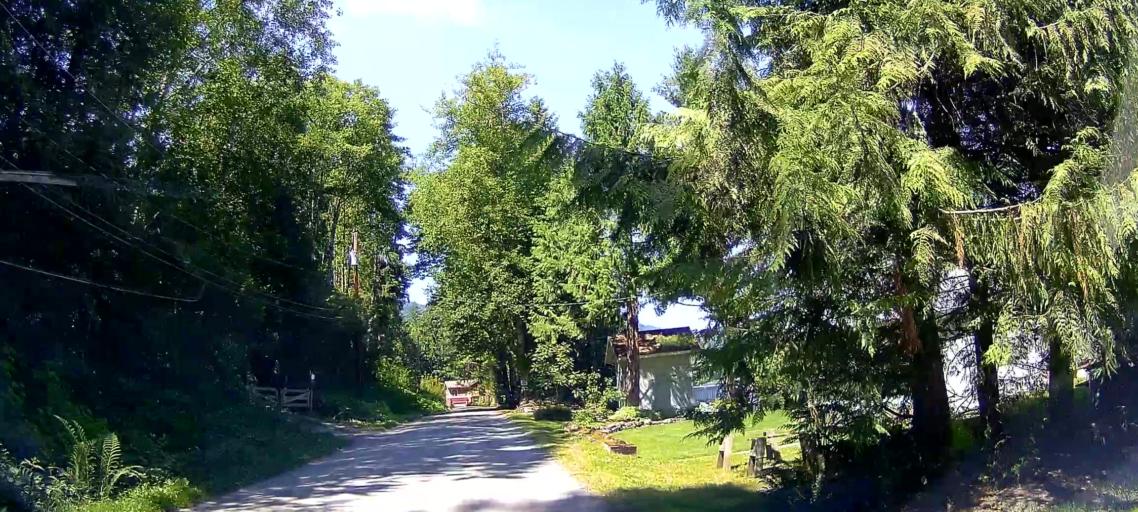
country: US
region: Washington
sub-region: Whatcom County
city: Sudden Valley
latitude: 48.6462
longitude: -122.3302
